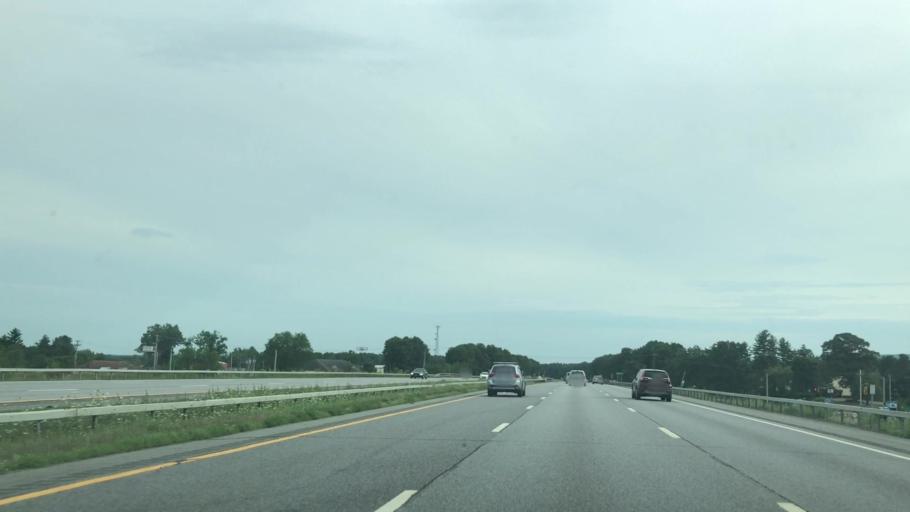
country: US
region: New York
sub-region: Warren County
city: West Glens Falls
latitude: 43.2994
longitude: -73.6787
